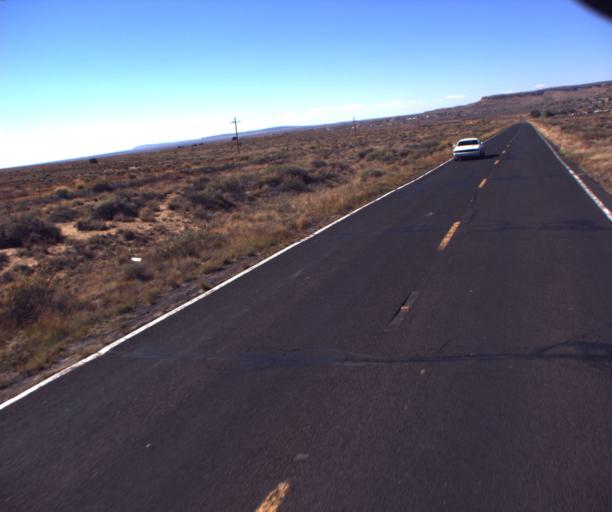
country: US
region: Arizona
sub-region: Navajo County
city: First Mesa
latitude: 35.8731
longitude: -110.5846
